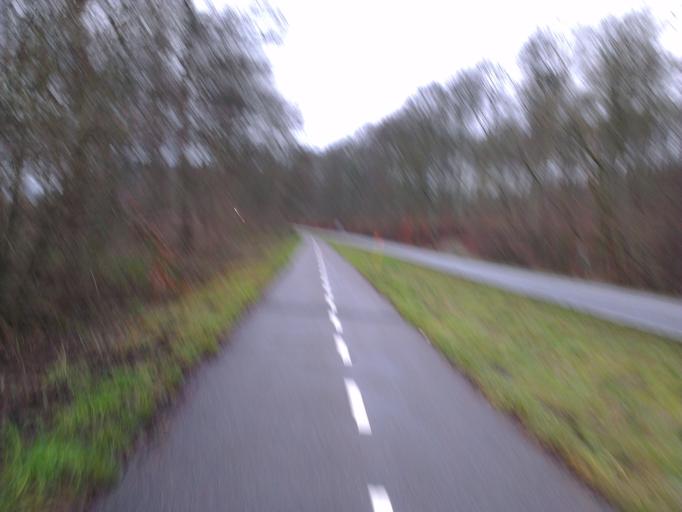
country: DK
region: Capital Region
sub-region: Frederikssund Kommune
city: Jaegerspris
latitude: 55.8540
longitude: 12.0172
